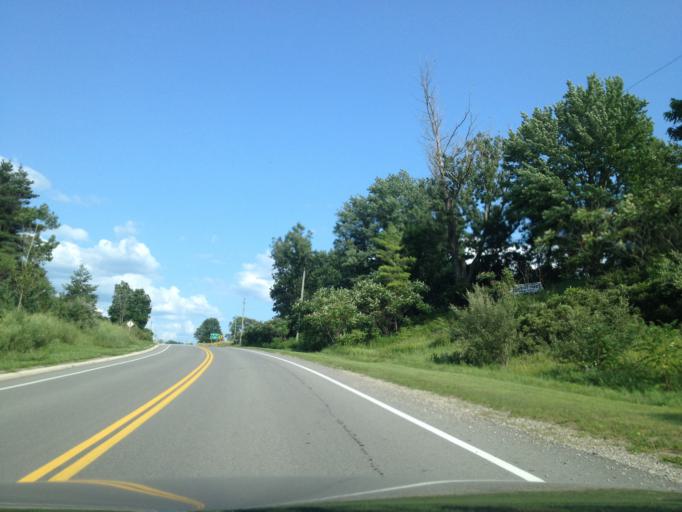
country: CA
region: Ontario
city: Aylmer
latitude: 42.7597
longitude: -80.8371
